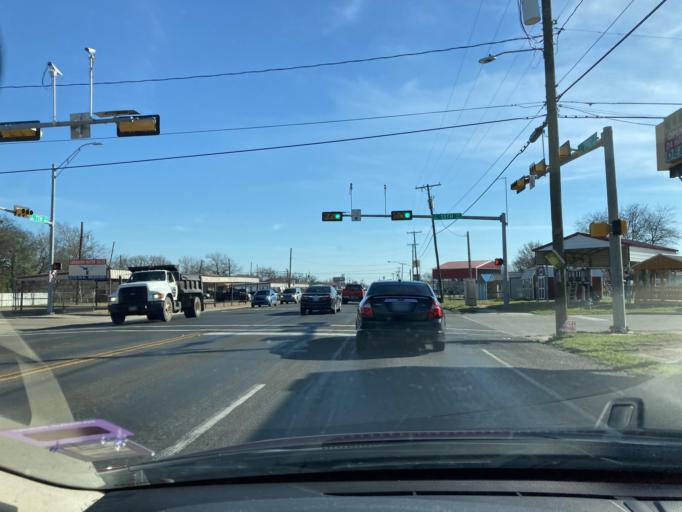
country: US
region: Texas
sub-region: Navarro County
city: Corsicana
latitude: 32.0892
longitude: -96.4562
